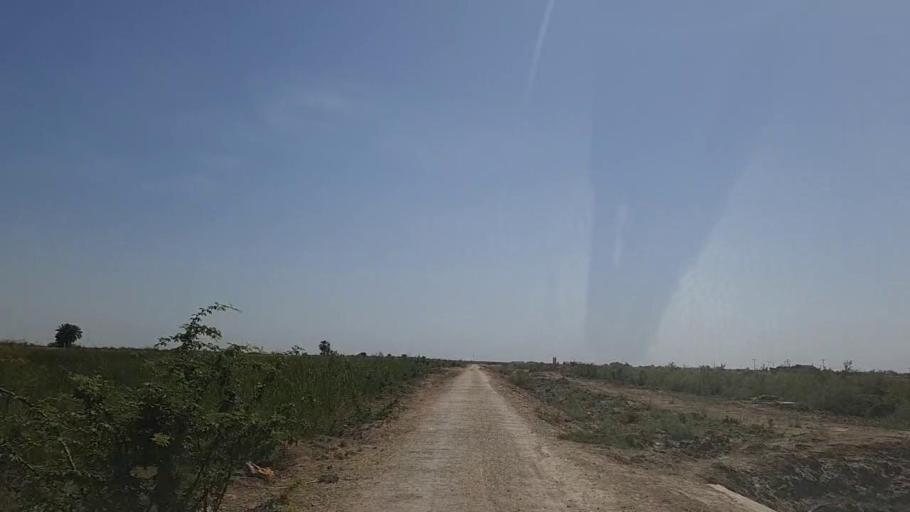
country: PK
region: Sindh
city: Thatta
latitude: 24.7843
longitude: 67.7555
